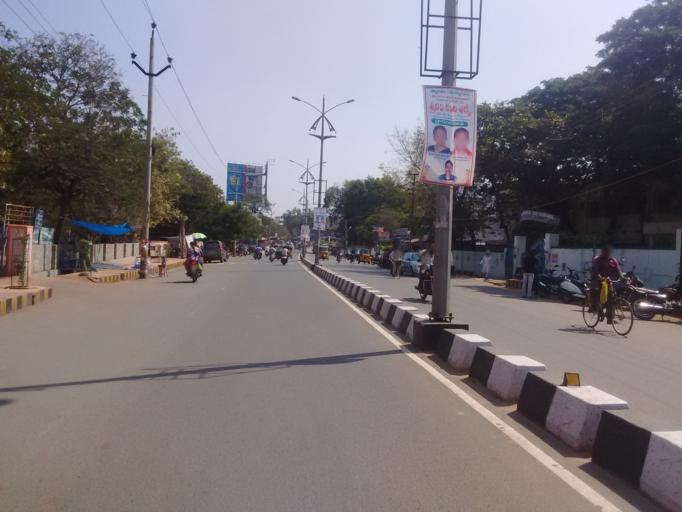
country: IN
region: Telangana
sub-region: Mahbubnagar
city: Alampur
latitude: 15.8325
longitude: 78.0434
